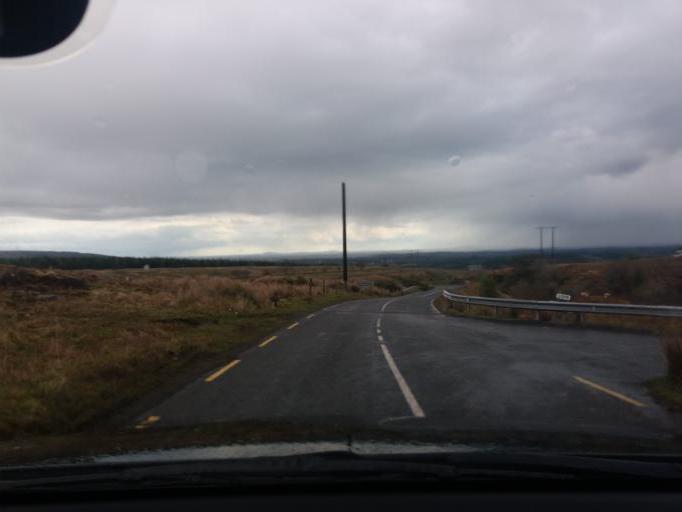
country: IE
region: Ulster
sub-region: An Cabhan
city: Ballyconnell
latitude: 54.1634
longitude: -7.7854
